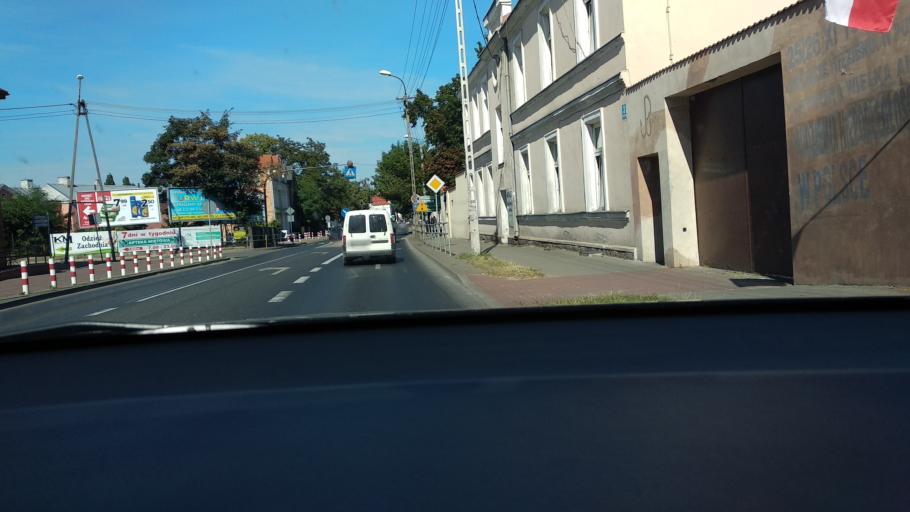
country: PL
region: Masovian Voivodeship
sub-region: Powiat pultuski
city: Pultusk
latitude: 52.7029
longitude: 21.0858
